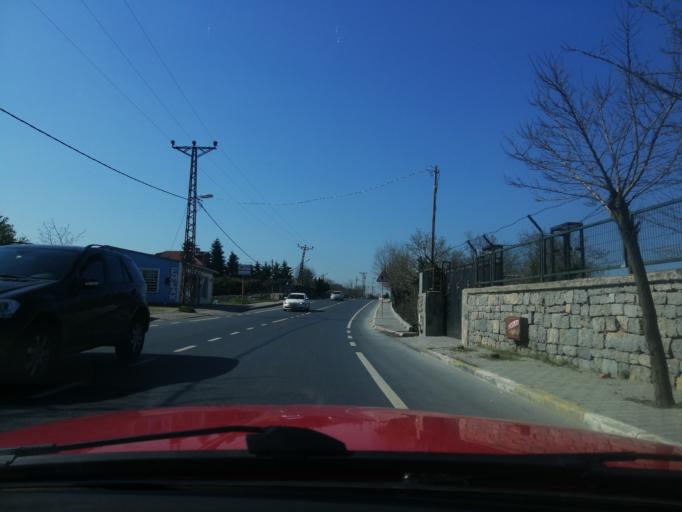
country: TR
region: Istanbul
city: Umraniye
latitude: 41.0710
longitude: 29.1610
